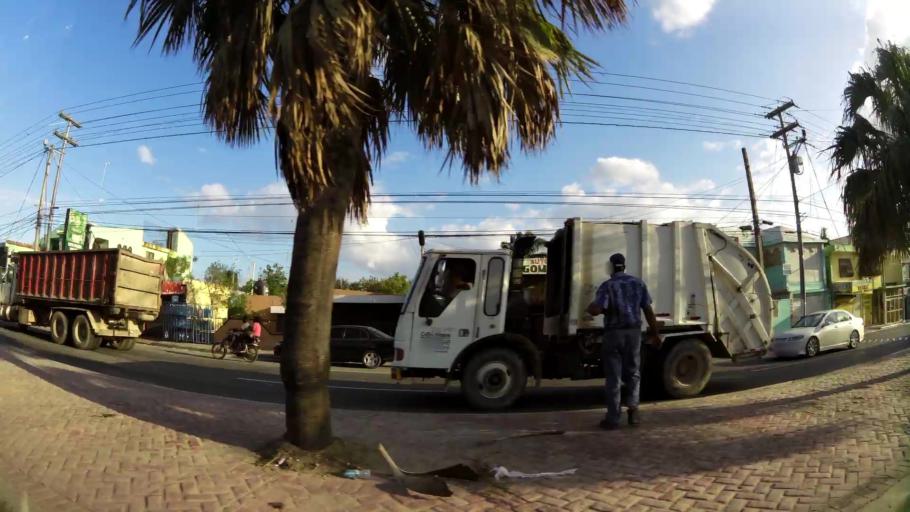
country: DO
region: Nacional
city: Ensanche Luperon
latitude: 18.5471
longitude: -69.9091
